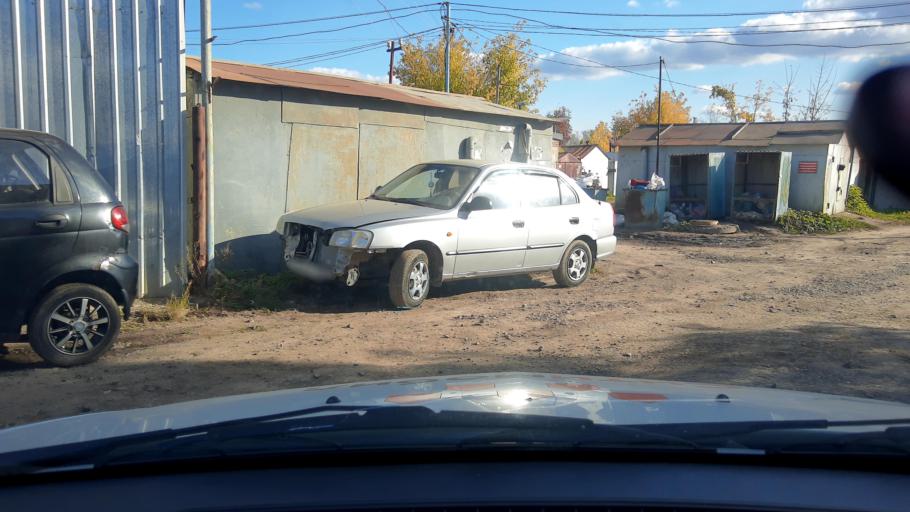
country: RU
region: Bashkortostan
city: Ufa
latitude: 54.7950
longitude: 56.0959
